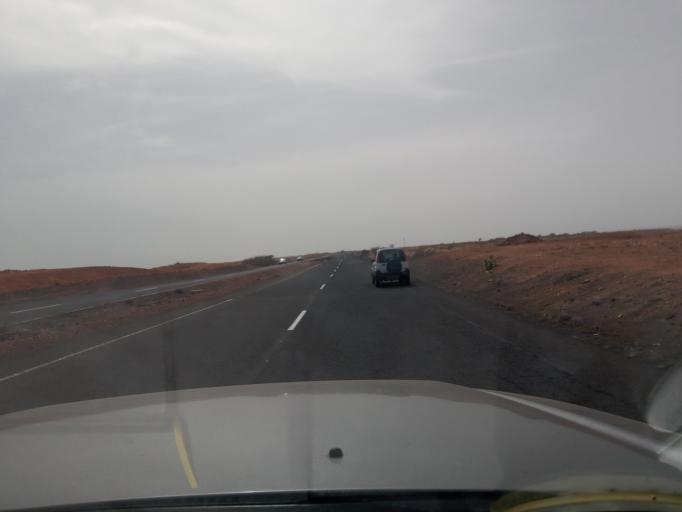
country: CV
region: Sal
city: Santa Maria
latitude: 16.6481
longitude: -22.9180
